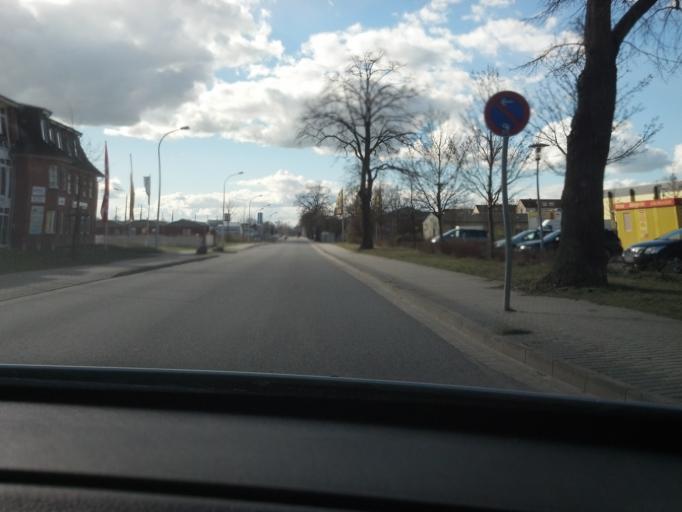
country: DE
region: Mecklenburg-Vorpommern
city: Neubrandenburg
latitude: 53.5608
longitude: 13.2800
